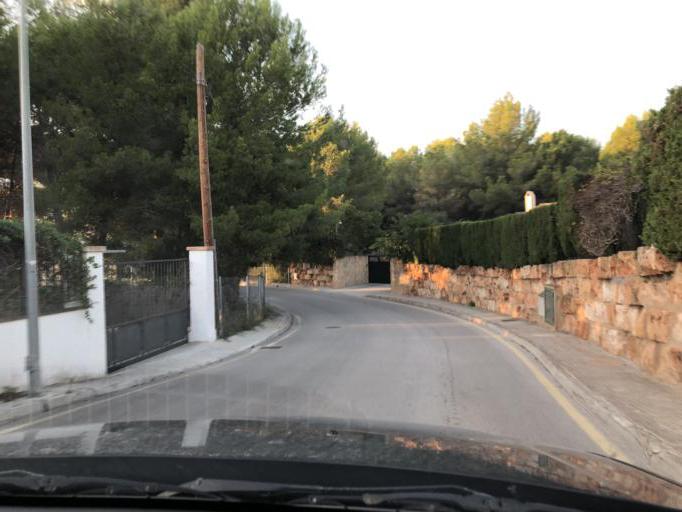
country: ES
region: Balearic Islands
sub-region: Illes Balears
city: Santa Ponsa
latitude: 39.5273
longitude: 2.4800
